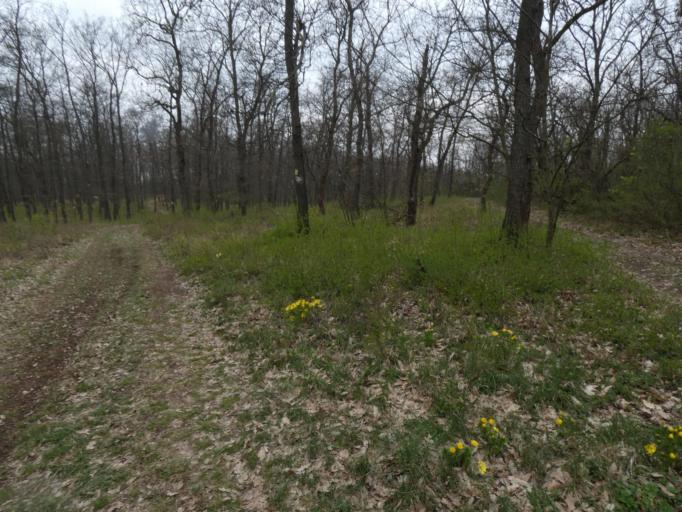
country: HU
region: Fejer
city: Bicske
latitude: 47.5110
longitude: 18.5719
